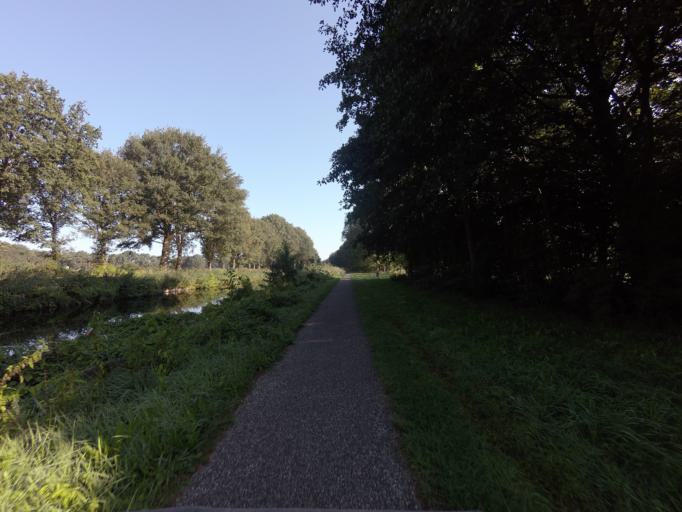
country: NL
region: Overijssel
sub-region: Gemeente Raalte
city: Raalte
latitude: 52.3396
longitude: 6.2708
